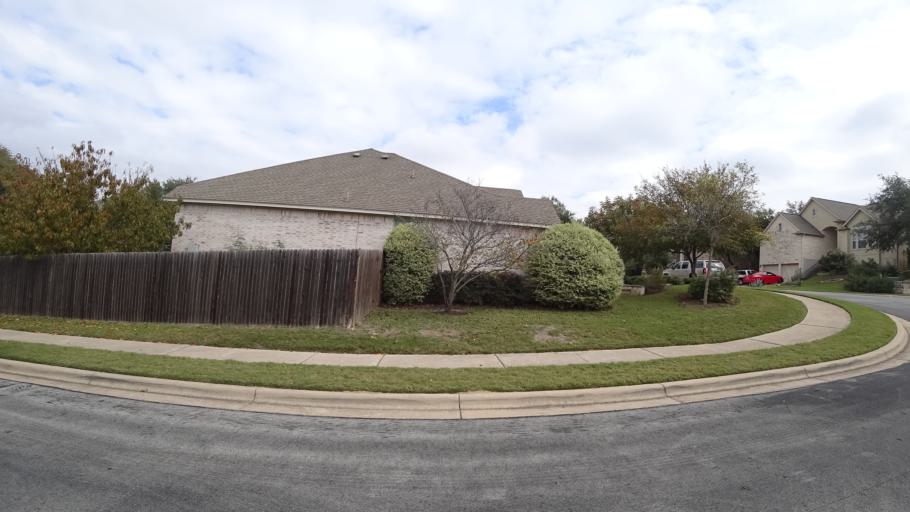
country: US
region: Texas
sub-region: Travis County
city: Shady Hollow
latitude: 30.2172
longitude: -97.8881
